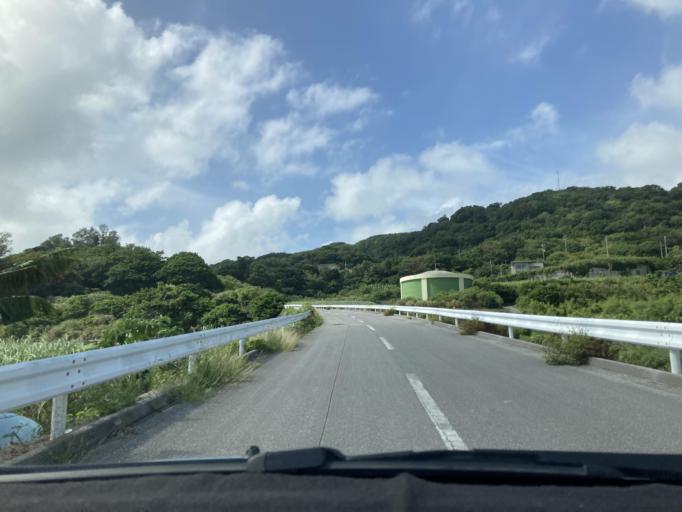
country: JP
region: Okinawa
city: Ginowan
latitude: 26.1522
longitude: 127.8055
